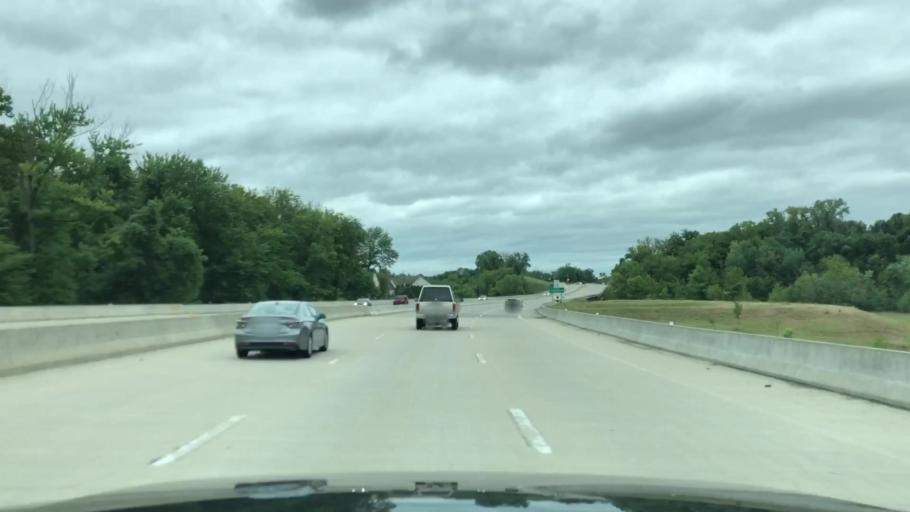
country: US
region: Missouri
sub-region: Saint Louis County
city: Maryland Heights
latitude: 38.6891
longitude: -90.4963
